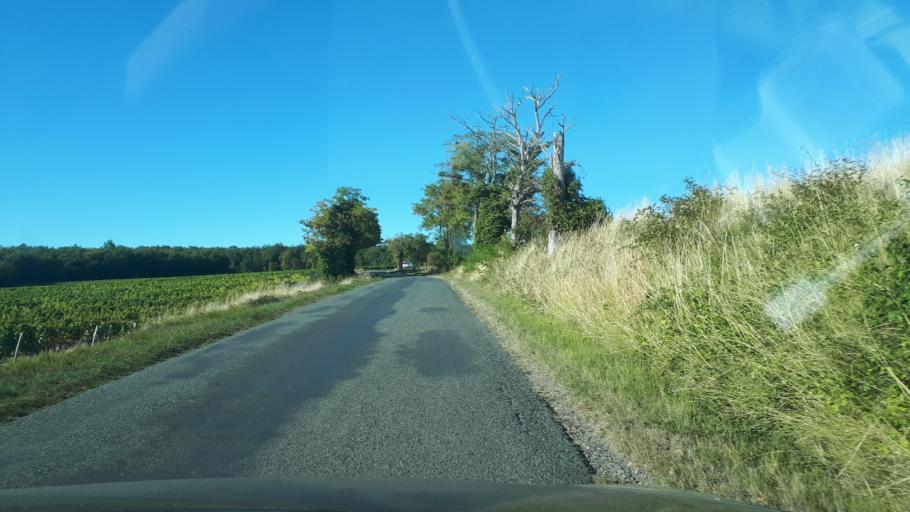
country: FR
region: Centre
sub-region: Departement du Cher
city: Sancerre
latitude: 47.2629
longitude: 2.7554
